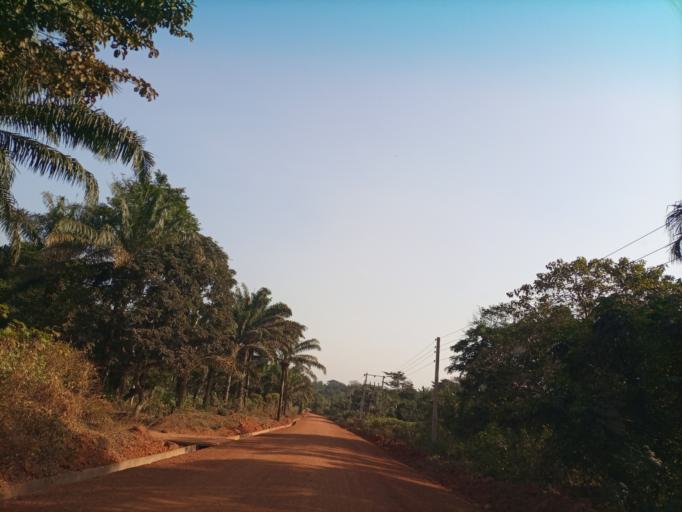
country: NG
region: Enugu
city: Opi
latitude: 6.7696
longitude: 7.3923
